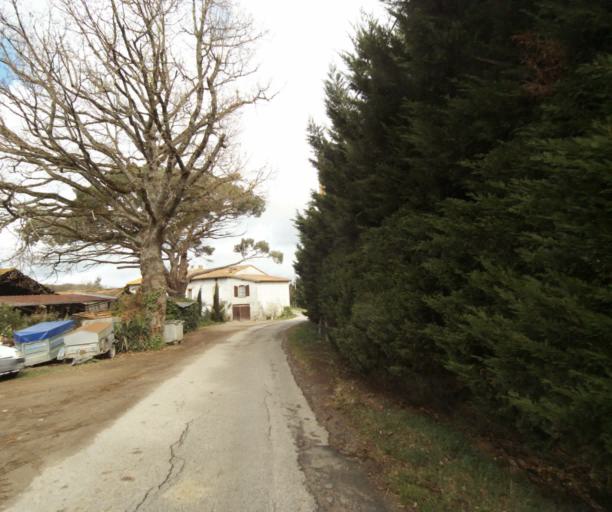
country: FR
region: Midi-Pyrenees
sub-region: Departement de l'Ariege
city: Saverdun
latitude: 43.2187
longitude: 1.5608
